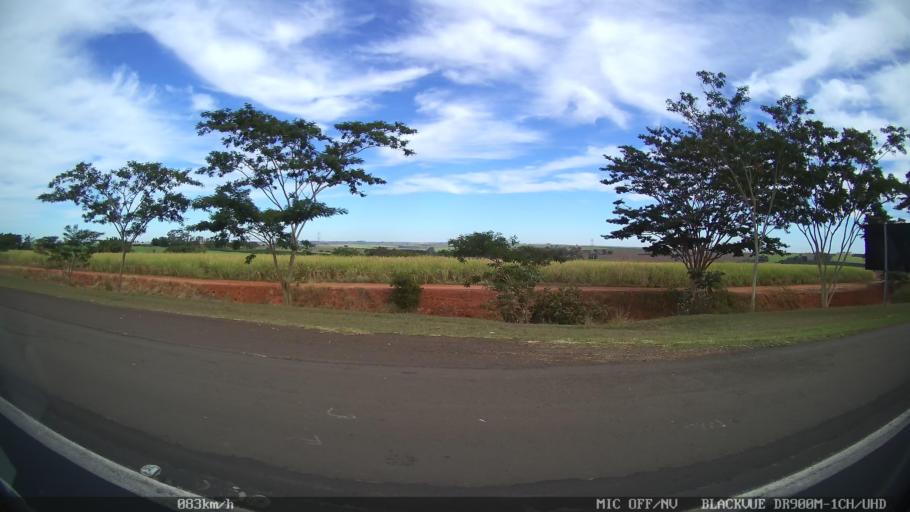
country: BR
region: Sao Paulo
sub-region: Santa Adelia
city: Santa Adelia
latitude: -21.3814
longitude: -48.7348
